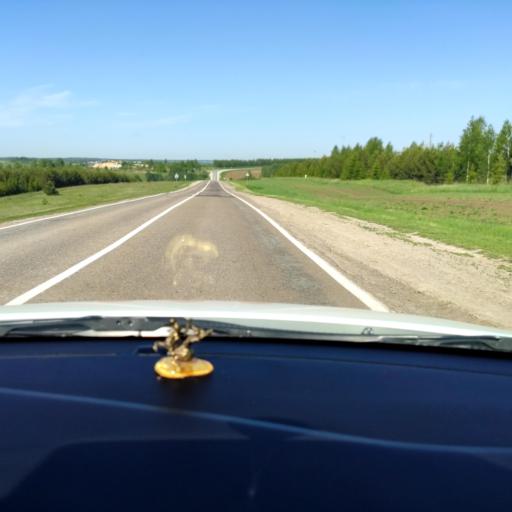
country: RU
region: Tatarstan
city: Vysokaya Gora
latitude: 56.0176
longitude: 49.2772
